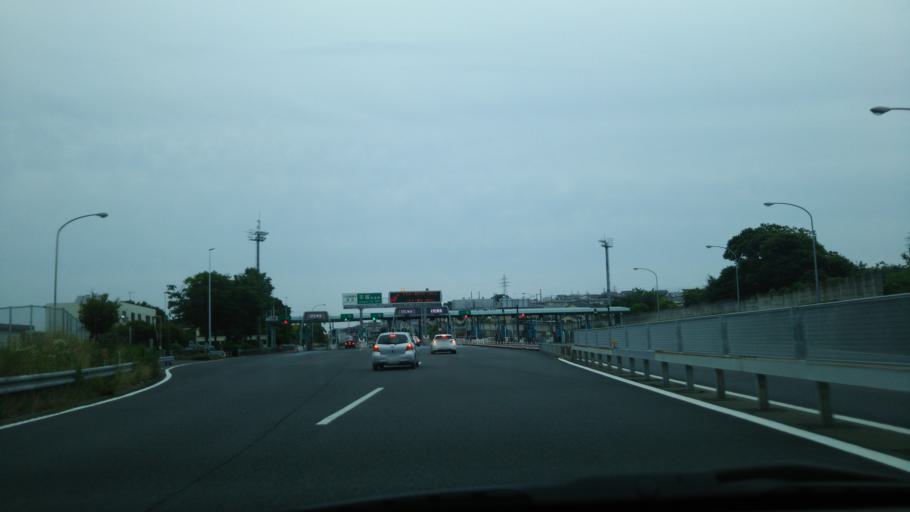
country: JP
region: Kanagawa
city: Oiso
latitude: 35.3356
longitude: 139.2947
